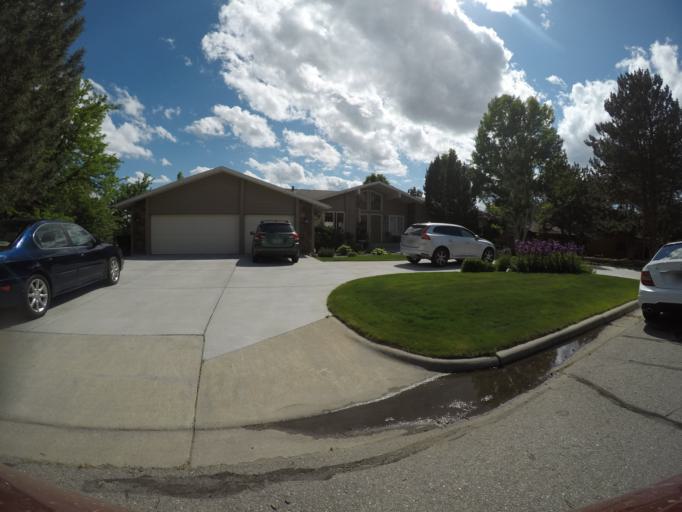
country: US
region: Montana
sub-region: Yellowstone County
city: Billings
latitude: 45.8084
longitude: -108.6550
